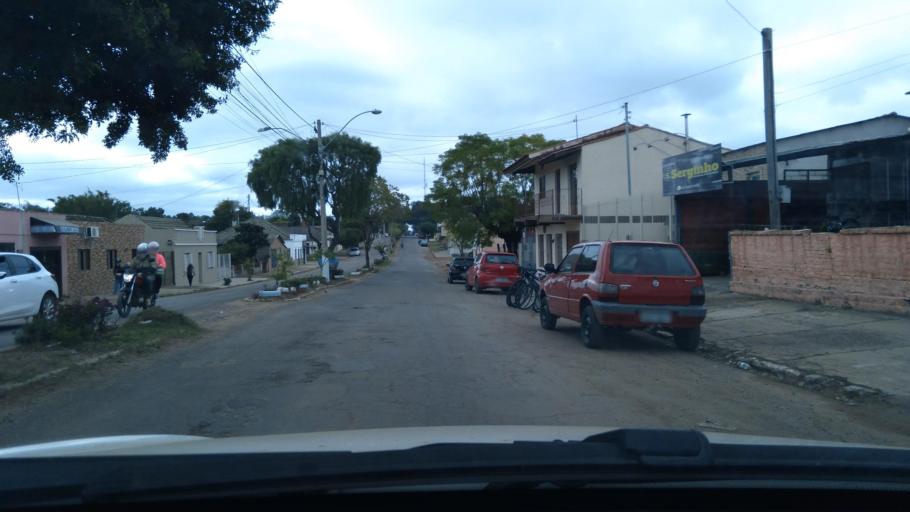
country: BR
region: Rio Grande do Sul
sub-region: Dom Pedrito
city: Dom Pedrito
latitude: -30.9719
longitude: -54.6735
